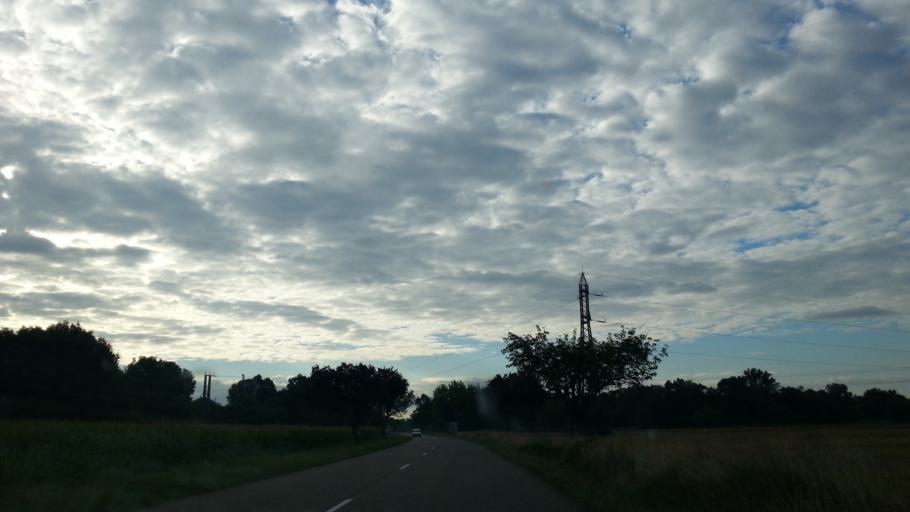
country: FR
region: Alsace
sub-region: Departement du Bas-Rhin
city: Gerstheim
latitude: 48.4044
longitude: 7.7165
